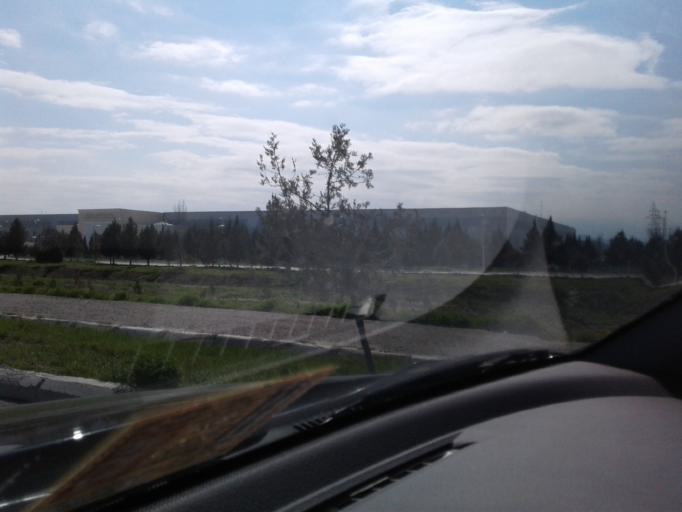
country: TM
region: Ahal
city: Abadan
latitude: 38.0665
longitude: 58.2526
